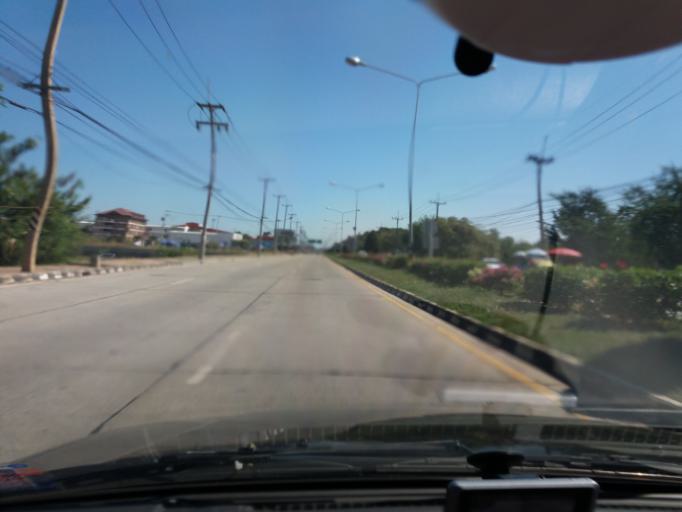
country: TH
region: Suphan Buri
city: Suphan Buri
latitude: 14.4642
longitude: 100.1367
